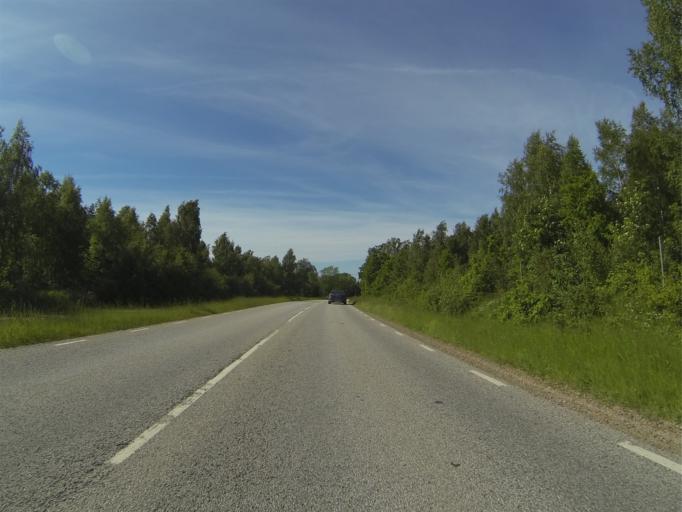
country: SE
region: Skane
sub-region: Lunds Kommun
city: Genarp
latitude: 55.7006
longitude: 13.3457
